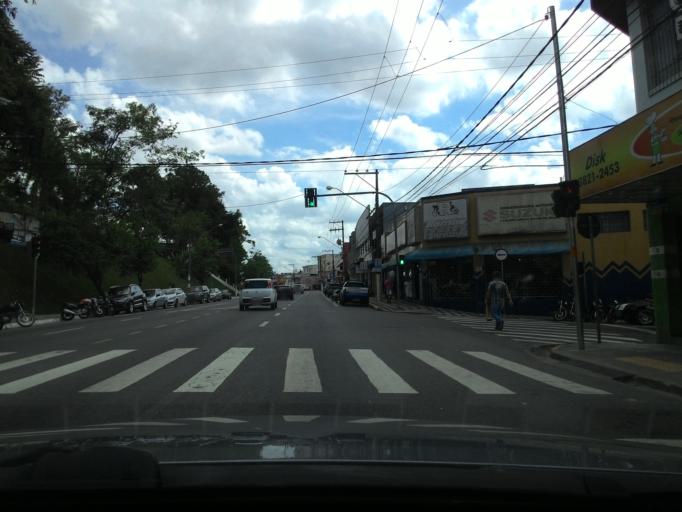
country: BR
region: Sao Paulo
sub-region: Registro
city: Registro
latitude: -24.4972
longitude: -47.8489
